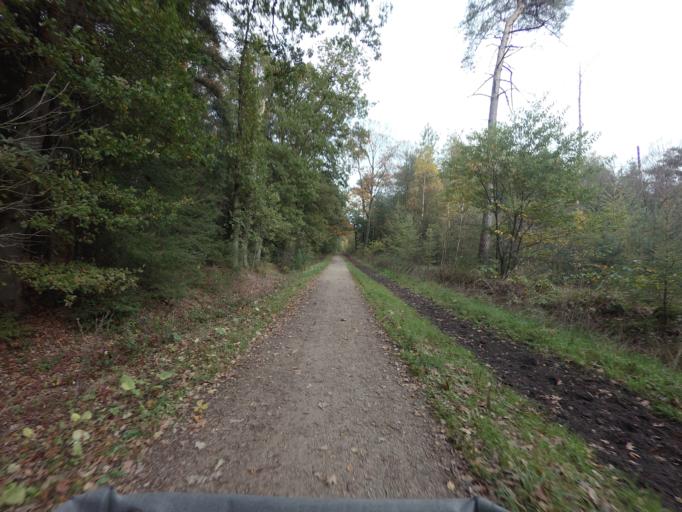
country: NL
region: North Holland
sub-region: Gemeente Hilversum
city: Hilversum
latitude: 52.1919
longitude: 5.2047
